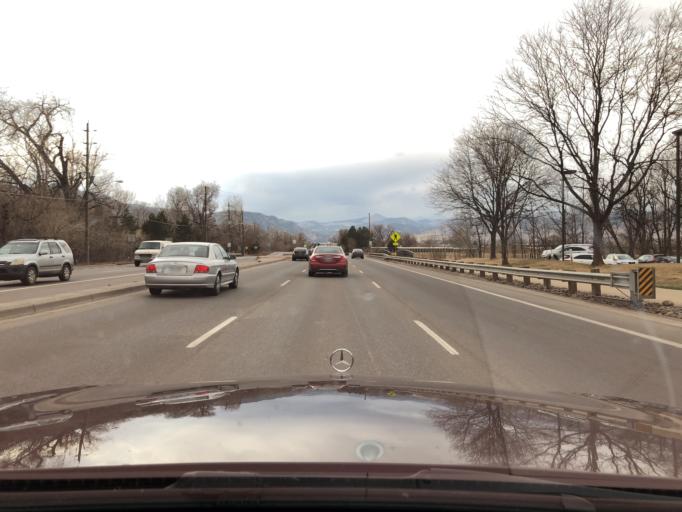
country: US
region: Colorado
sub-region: Boulder County
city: Boulder
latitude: 40.0148
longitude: -105.2135
